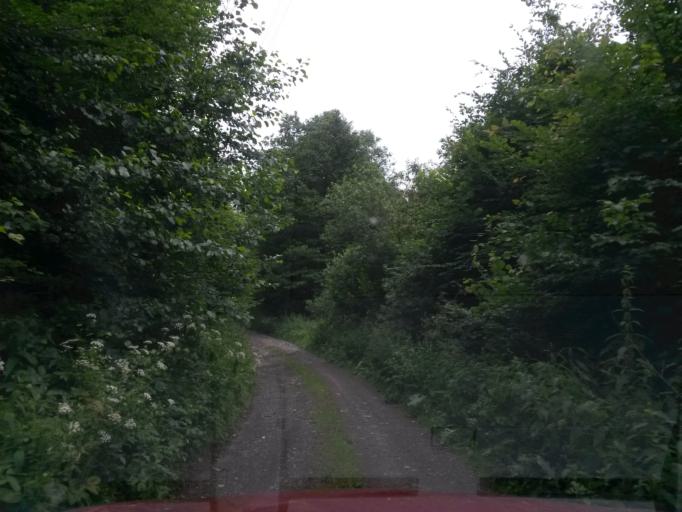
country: SK
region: Banskobystricky
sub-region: Okres Banska Bystrica
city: Zvolen
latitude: 48.5036
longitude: 19.2611
